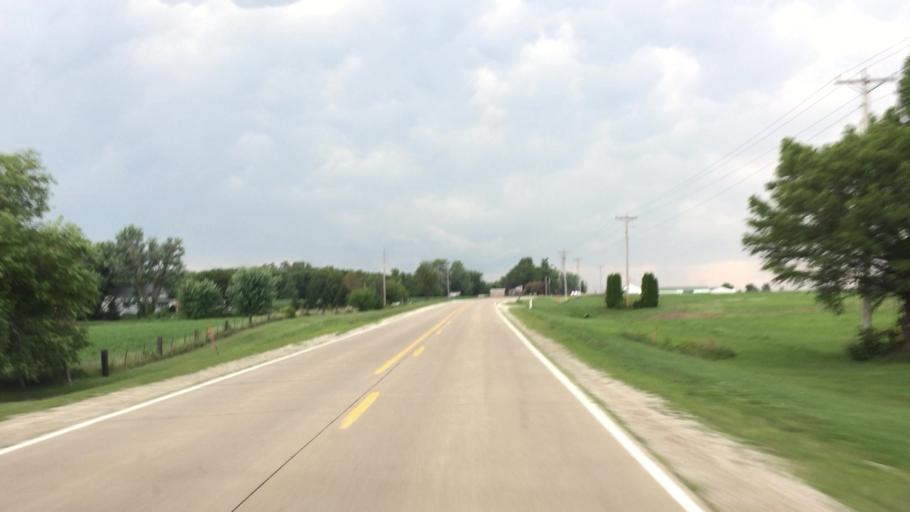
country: US
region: Iowa
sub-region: Lee County
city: Fort Madison
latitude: 40.7305
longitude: -91.3296
